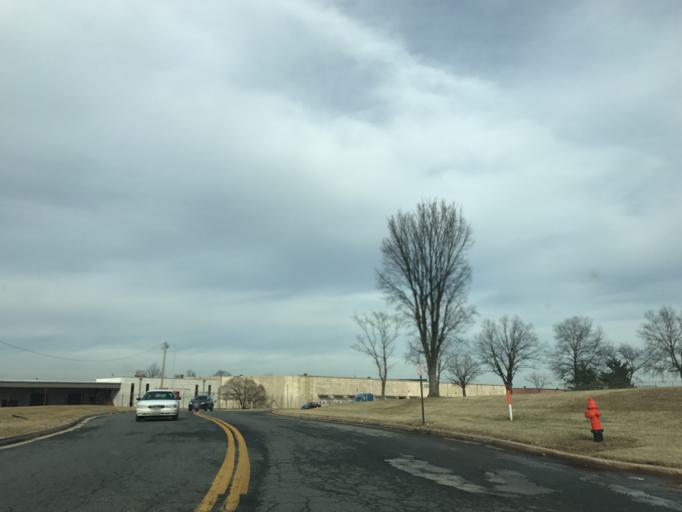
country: US
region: Maryland
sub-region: Baltimore County
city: Rosedale
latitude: 39.2966
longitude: -76.5225
